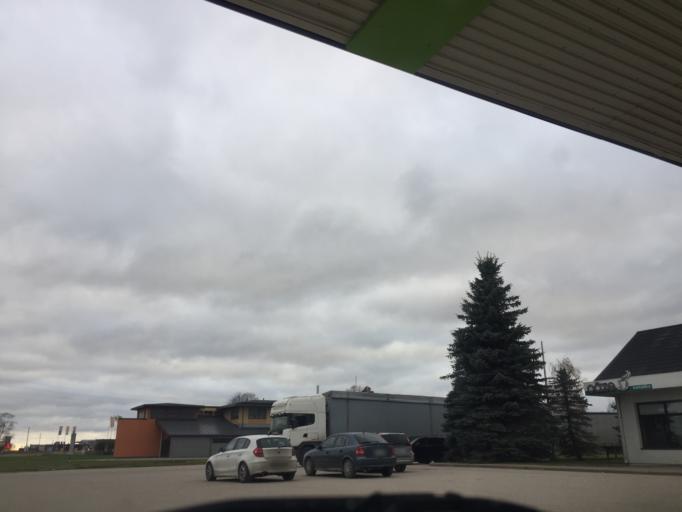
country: LV
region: Saldus Rajons
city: Saldus
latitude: 56.6830
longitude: 22.4769
